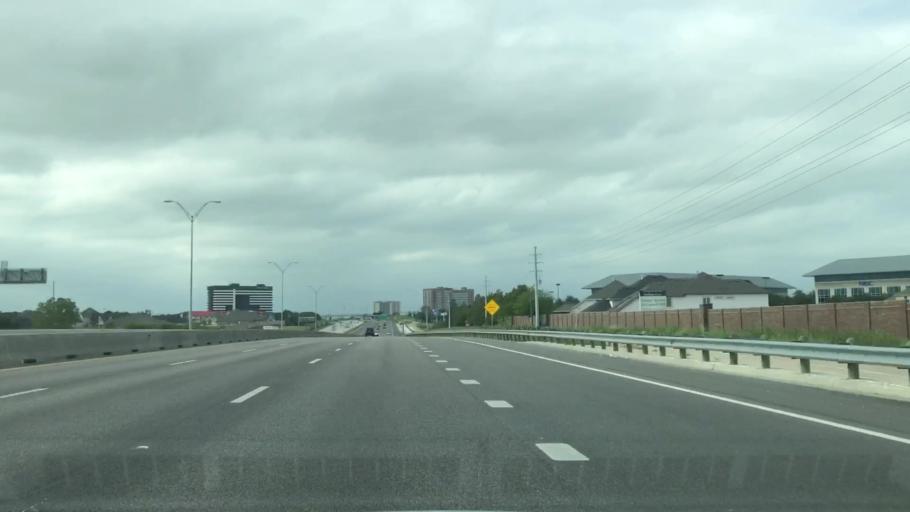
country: US
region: Texas
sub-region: Dallas County
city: Coppell
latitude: 32.9094
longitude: -96.9976
